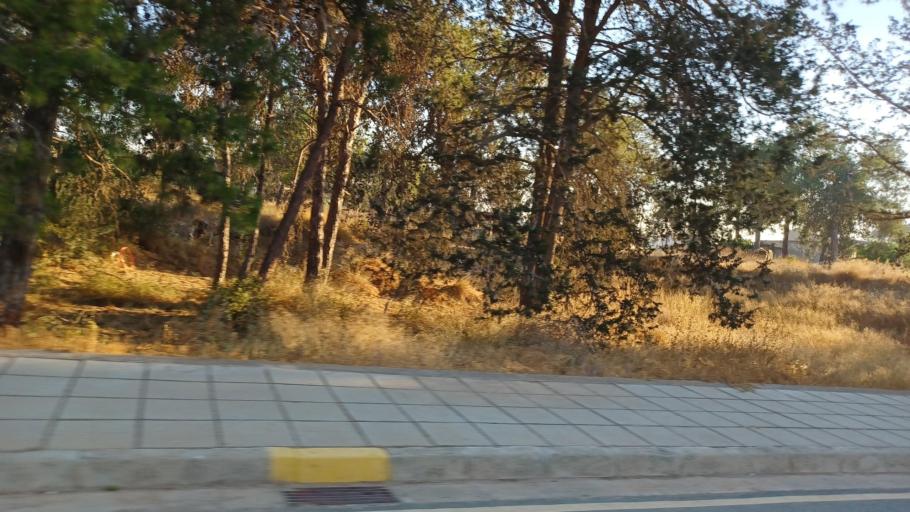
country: CY
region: Ammochostos
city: Achna
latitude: 35.0314
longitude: 33.7690
